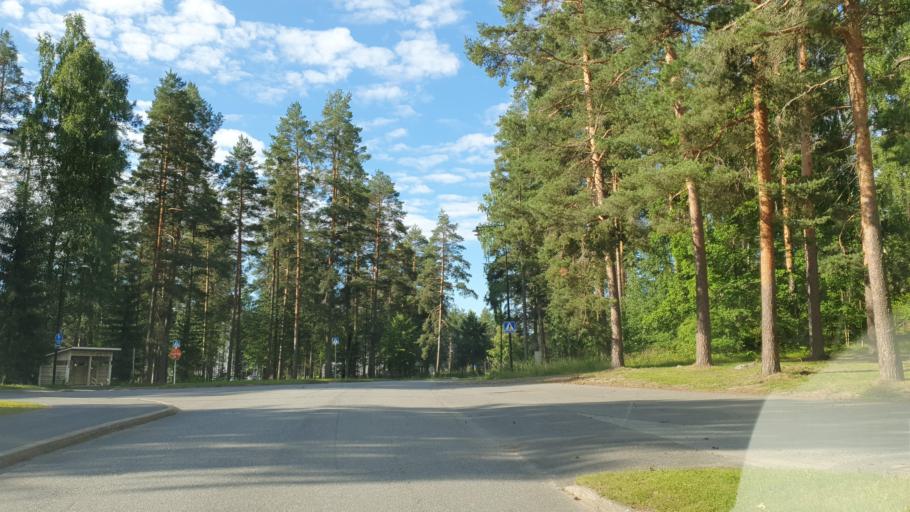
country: FI
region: Central Finland
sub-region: Jyvaeskylae
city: Saeynaetsalo
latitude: 62.1582
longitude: 25.7641
